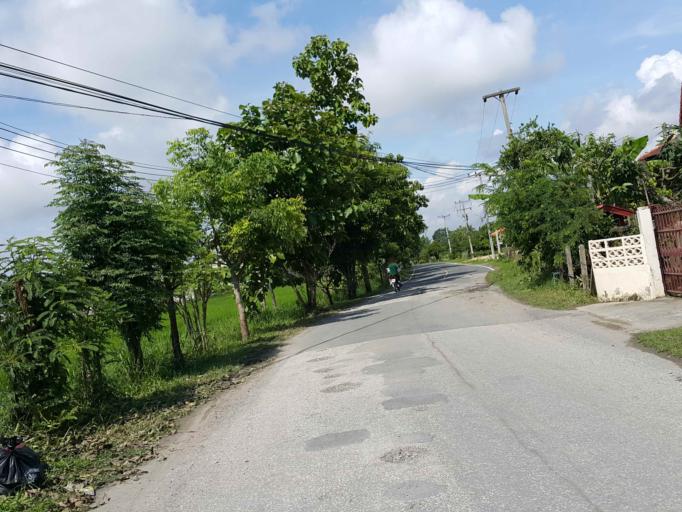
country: TH
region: Chiang Mai
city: San Sai
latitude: 18.8067
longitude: 99.0746
